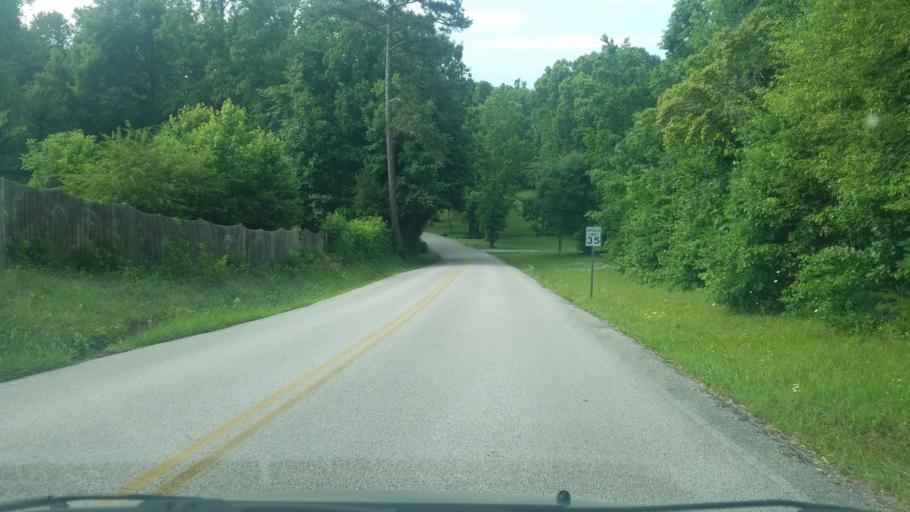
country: US
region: Tennessee
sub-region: Hamilton County
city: Collegedale
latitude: 35.0254
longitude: -85.0605
